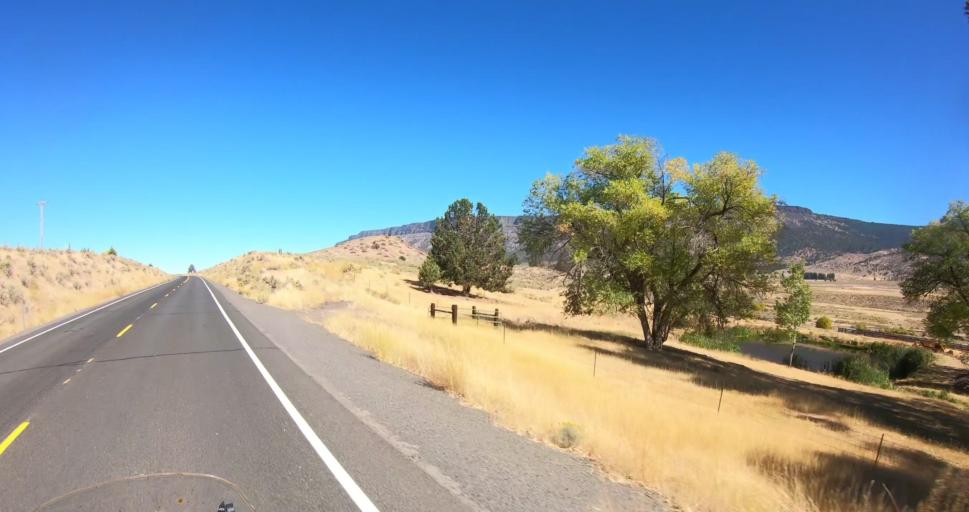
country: US
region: Oregon
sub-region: Lake County
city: Lakeview
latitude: 42.4363
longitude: -120.2809
